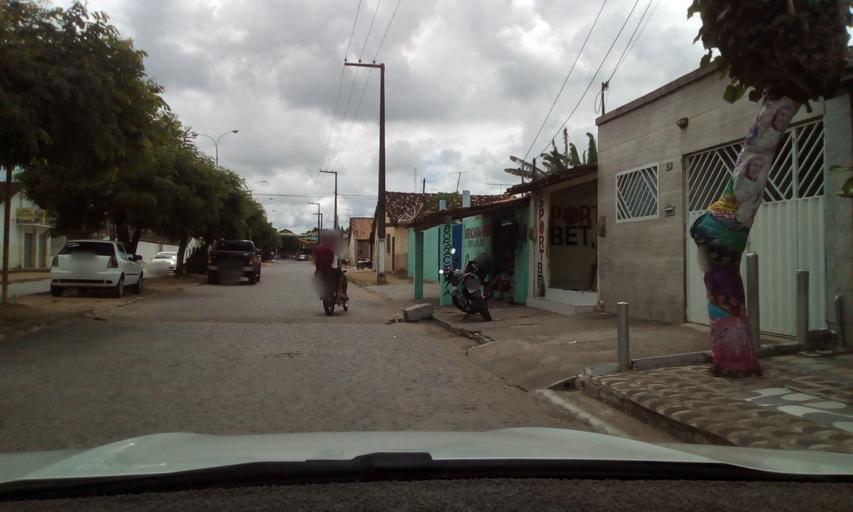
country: BR
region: Paraiba
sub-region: Rio Tinto
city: Rio Tinto
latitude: -6.7881
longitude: -35.0665
